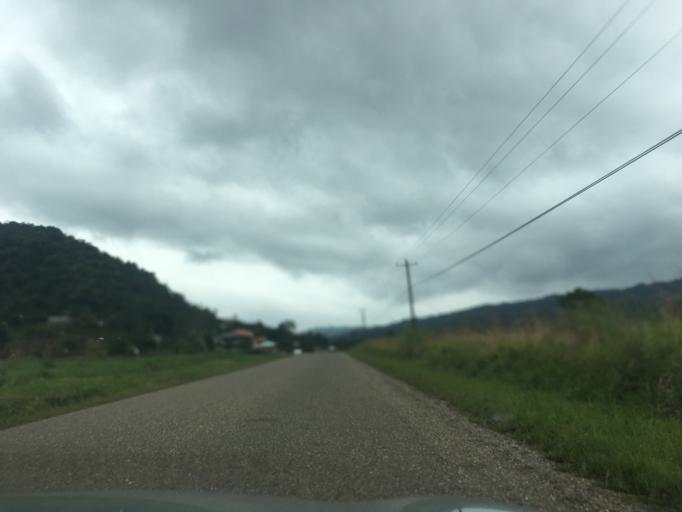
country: BZ
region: Stann Creek
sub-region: Dangriga
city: Dangriga
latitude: 17.0322
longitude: -88.5173
